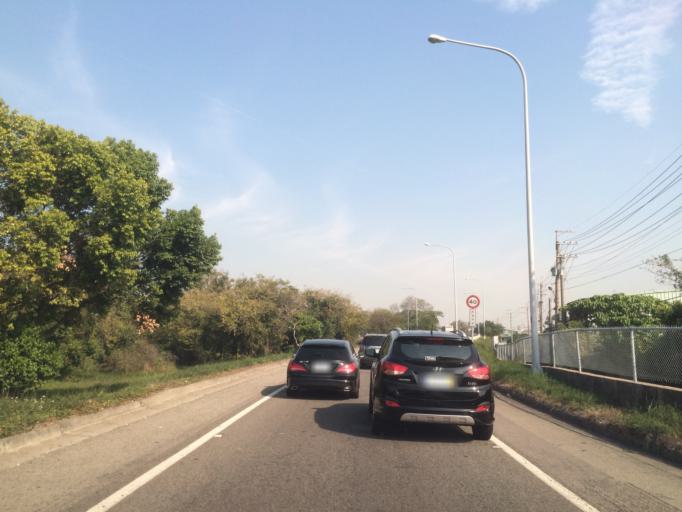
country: TW
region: Taiwan
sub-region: Taichung City
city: Taichung
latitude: 24.2036
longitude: 120.6573
